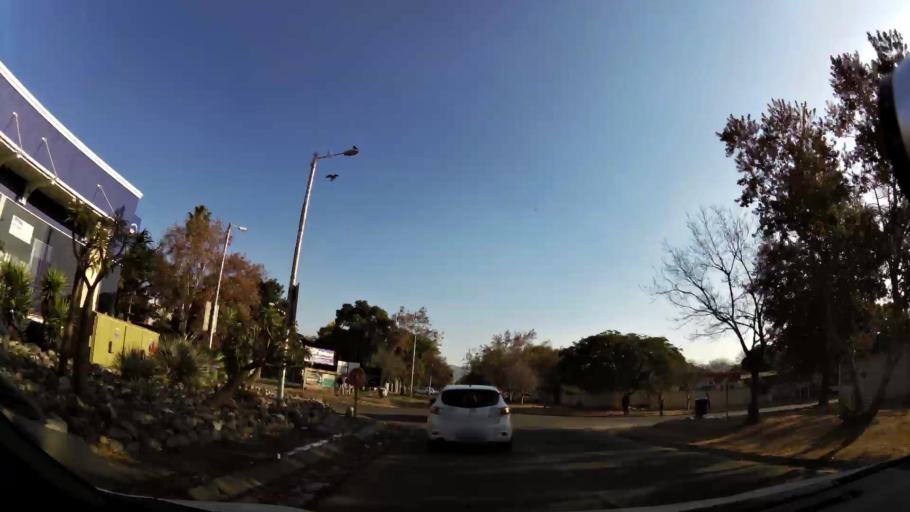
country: ZA
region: North-West
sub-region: Bojanala Platinum District Municipality
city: Rustenburg
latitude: -25.6746
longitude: 27.2381
